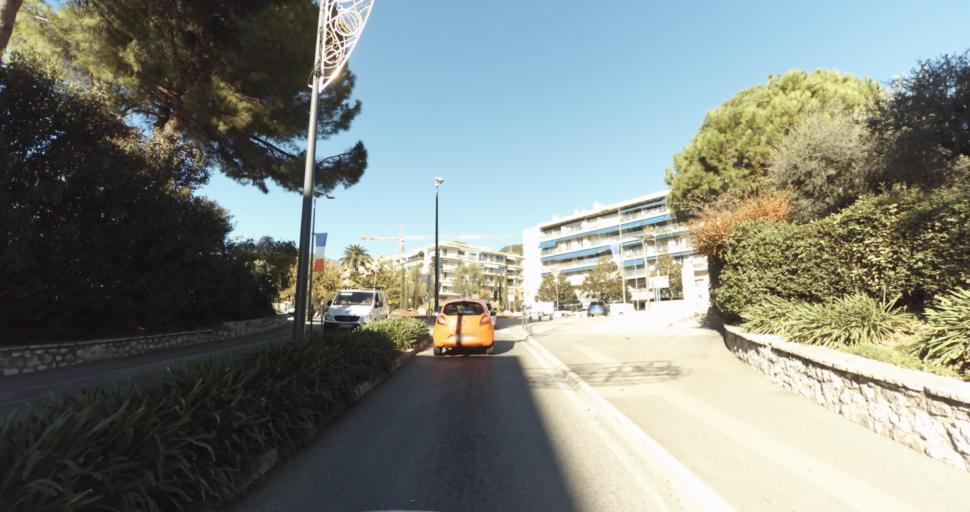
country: FR
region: Provence-Alpes-Cote d'Azur
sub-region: Departement des Alpes-Maritimes
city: Vence
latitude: 43.7226
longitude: 7.1078
